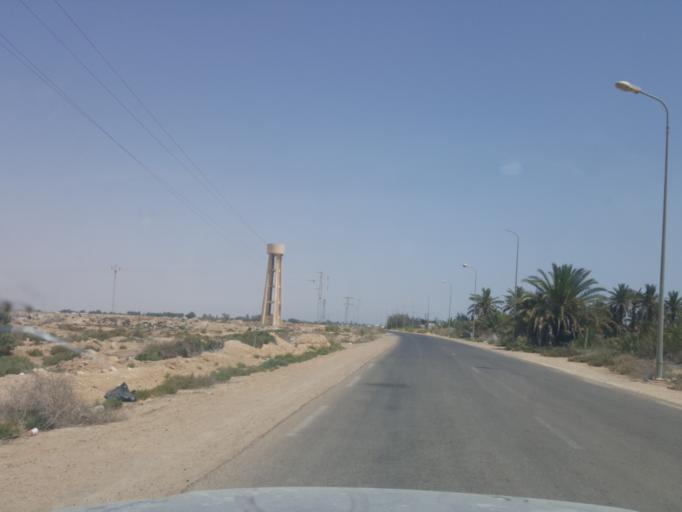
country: TN
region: Qabis
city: Gabes
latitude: 33.9707
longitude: 10.0005
